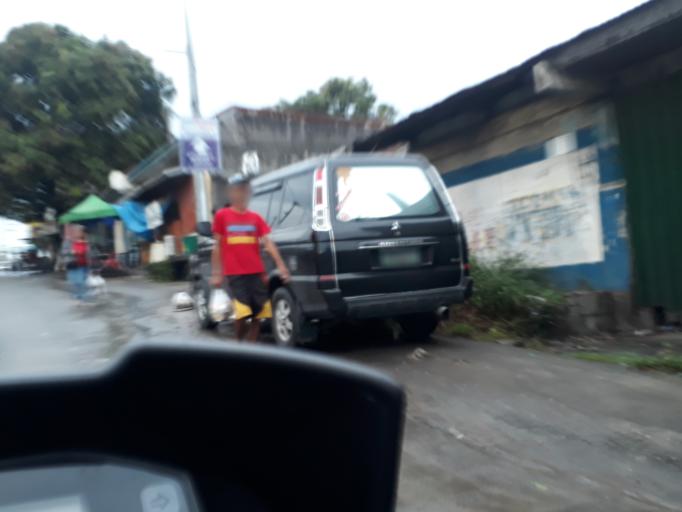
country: PH
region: Central Luzon
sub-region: Province of Bulacan
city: San Jose del Monte
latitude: 14.7717
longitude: 121.0502
